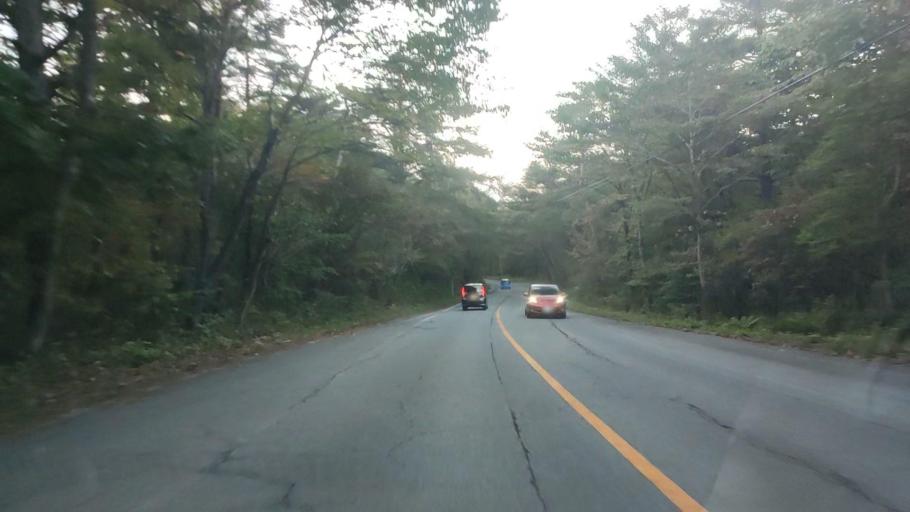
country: JP
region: Nagano
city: Komoro
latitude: 36.4059
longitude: 138.5699
